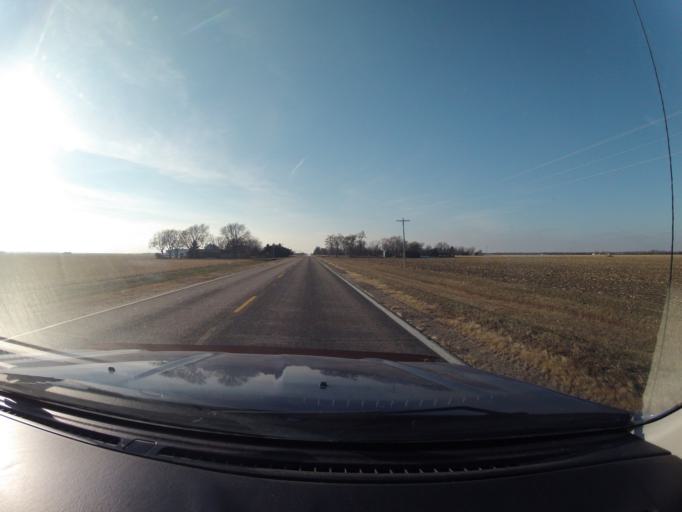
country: US
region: Nebraska
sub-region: Buffalo County
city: Kearney
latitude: 40.6410
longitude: -98.9947
